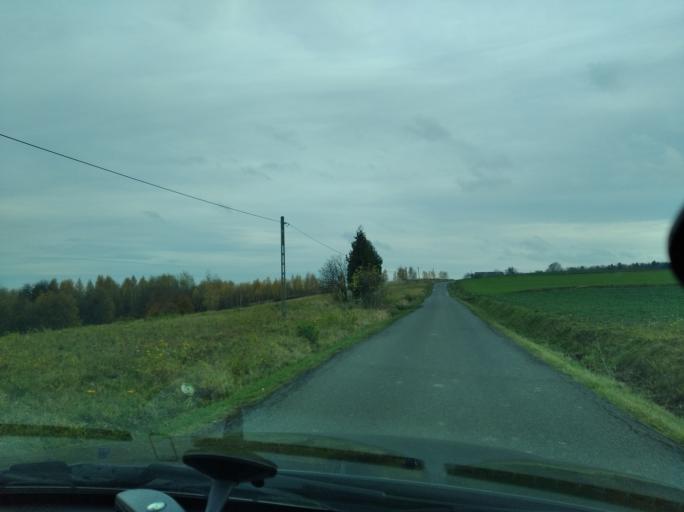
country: PL
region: Subcarpathian Voivodeship
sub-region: Powiat strzyzowski
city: Strzyzow
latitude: 49.9148
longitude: 21.7680
